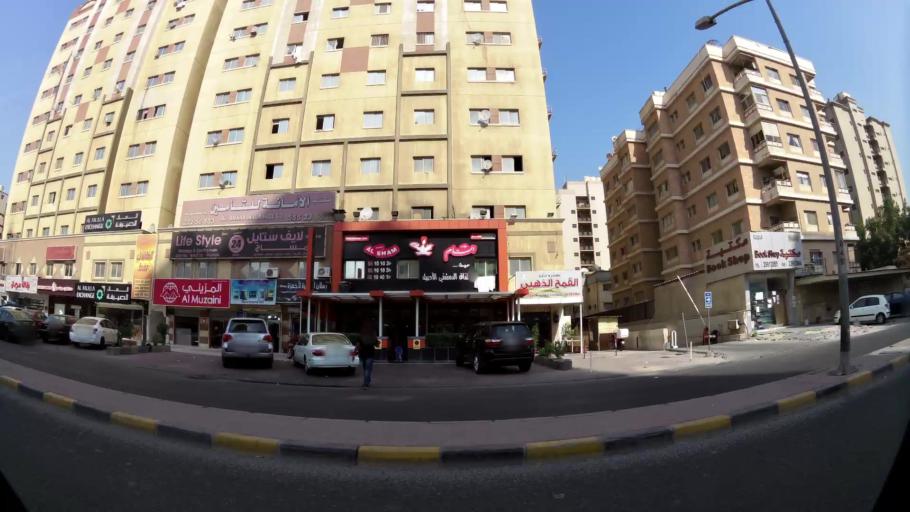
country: KW
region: Muhafazat Hawalli
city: As Salimiyah
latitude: 29.3254
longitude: 48.0579
